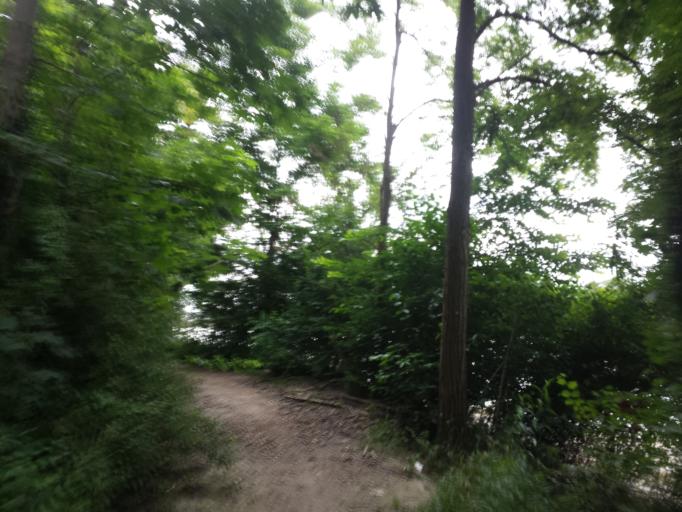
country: DE
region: Rheinland-Pfalz
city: Altrip
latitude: 49.4282
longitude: 8.5043
